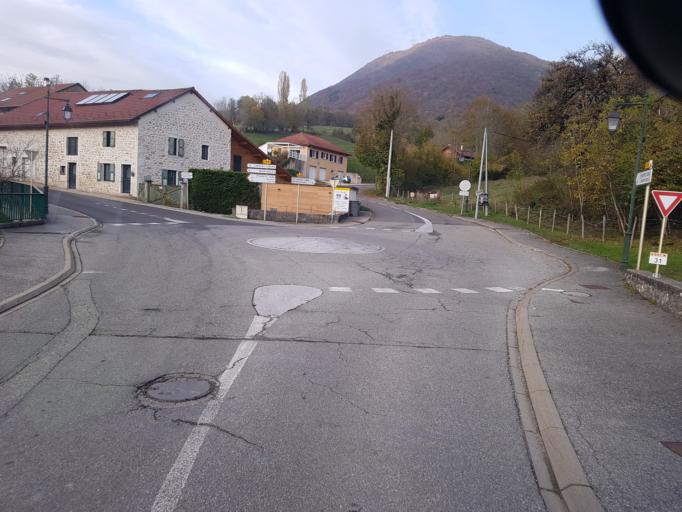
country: FR
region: Rhone-Alpes
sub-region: Departement de l'Ain
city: Chatillon-en-Michaille
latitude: 46.1510
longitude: 5.8227
